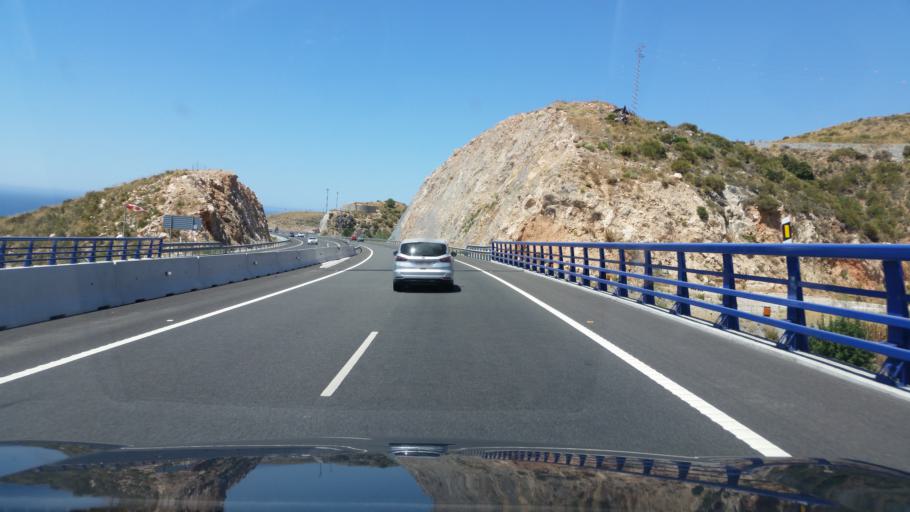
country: ES
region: Andalusia
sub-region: Provincia de Granada
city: Gualchos
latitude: 36.7149
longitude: -3.3964
